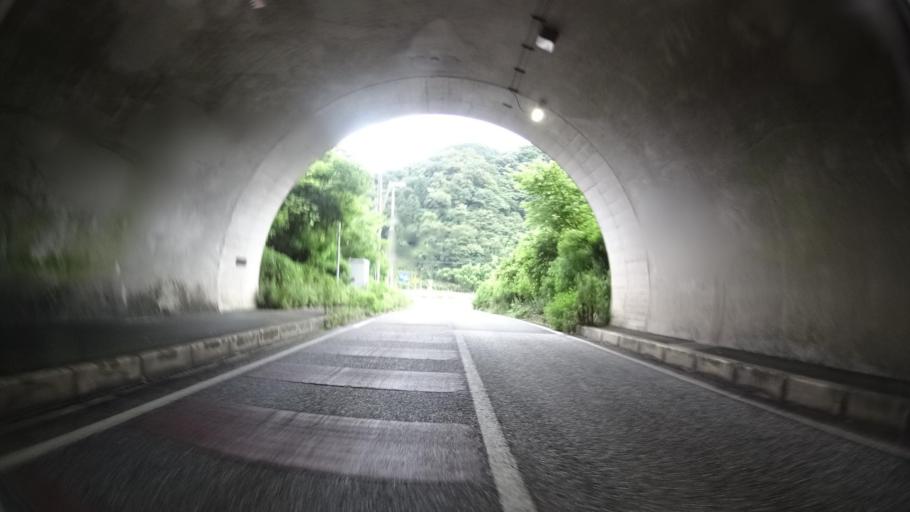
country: JP
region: Kyoto
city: Maizuru
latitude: 35.5217
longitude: 135.3543
